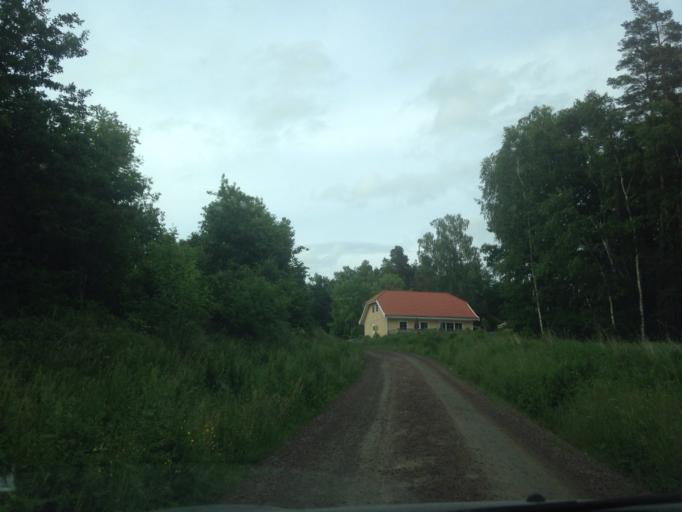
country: SE
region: Vaestra Goetaland
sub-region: Kungalvs Kommun
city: Kungalv
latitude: 57.8110
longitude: 11.9289
